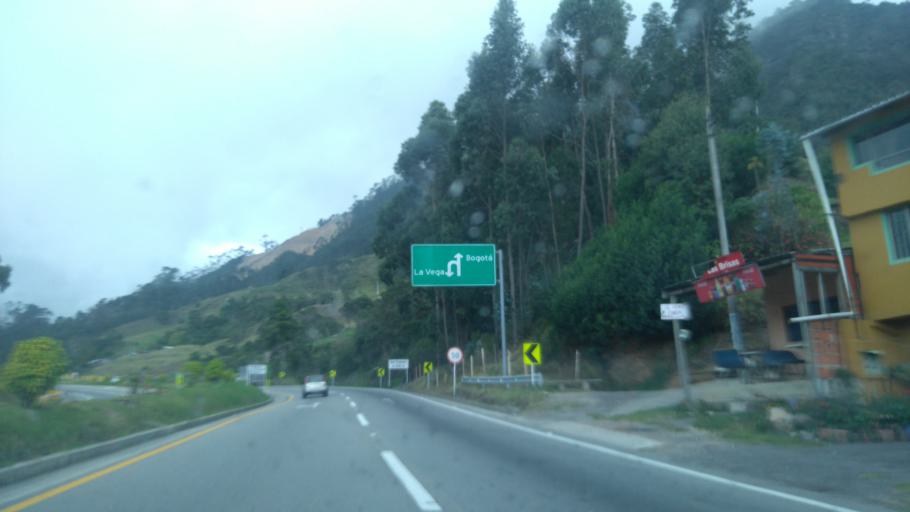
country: CO
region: Cundinamarca
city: El Rosal
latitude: 4.8829
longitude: -74.3003
